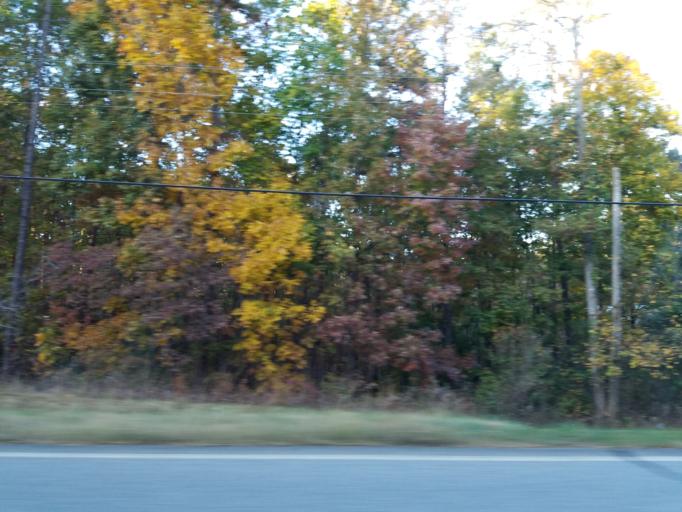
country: US
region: Georgia
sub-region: Lumpkin County
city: Dahlonega
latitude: 34.5488
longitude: -84.0938
